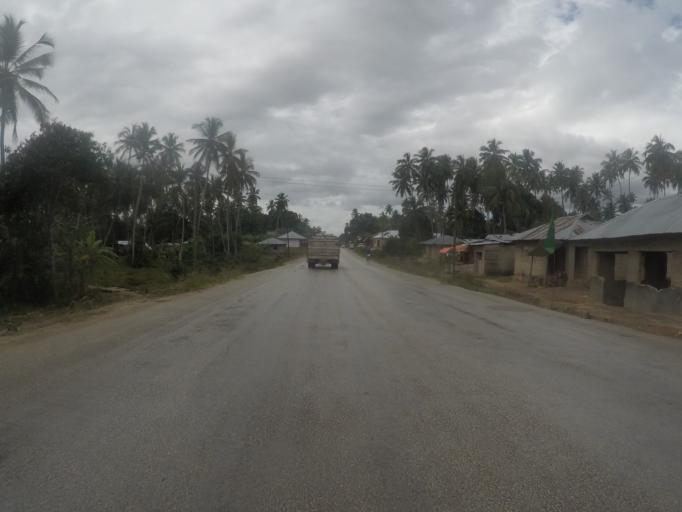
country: TZ
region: Zanzibar Central/South
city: Koani
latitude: -6.0255
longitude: 39.2390
